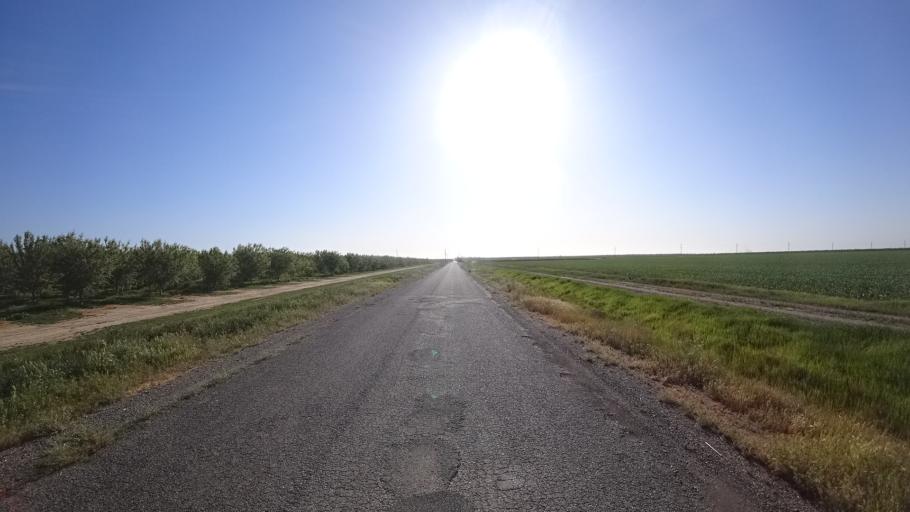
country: US
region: California
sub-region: Glenn County
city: Orland
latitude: 39.6822
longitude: -122.1825
